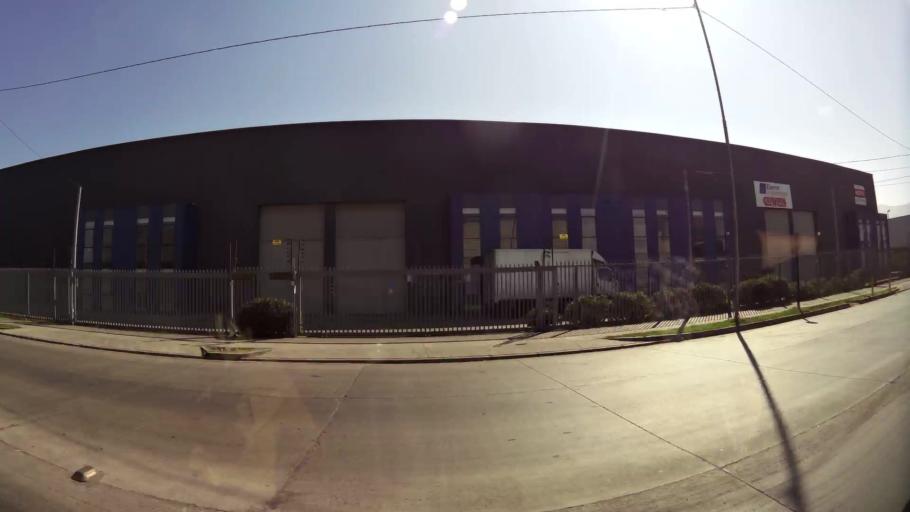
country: CL
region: Santiago Metropolitan
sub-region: Provincia de Chacabuco
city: Chicureo Abajo
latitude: -33.3631
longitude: -70.6806
